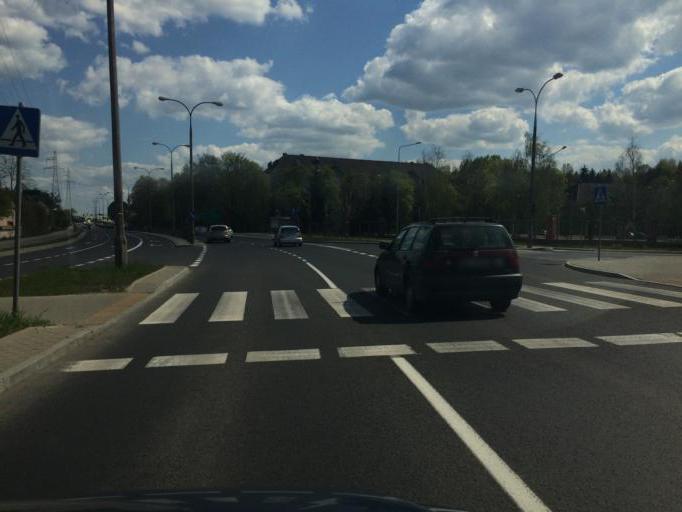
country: PL
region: Warmian-Masurian Voivodeship
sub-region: Olsztyn
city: Kortowo
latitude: 53.7690
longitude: 20.4591
